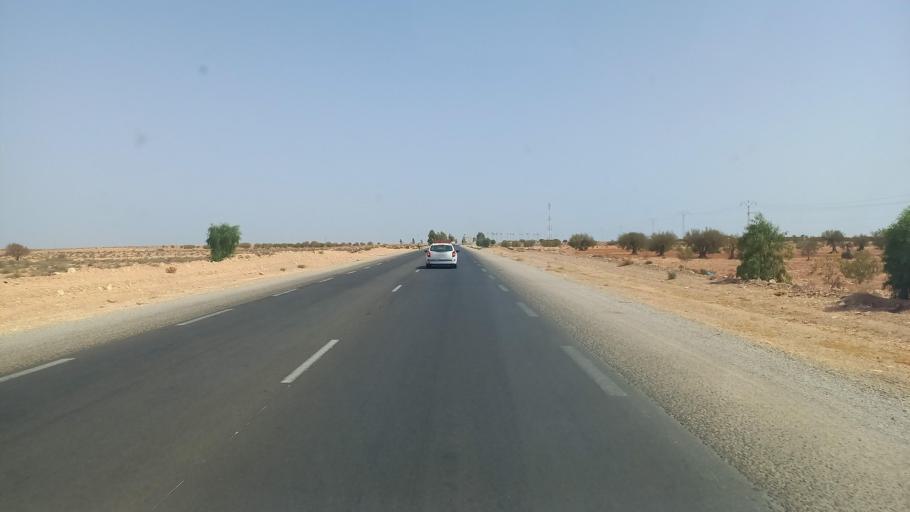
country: TN
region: Madanin
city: Medenine
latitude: 33.3804
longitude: 10.6987
